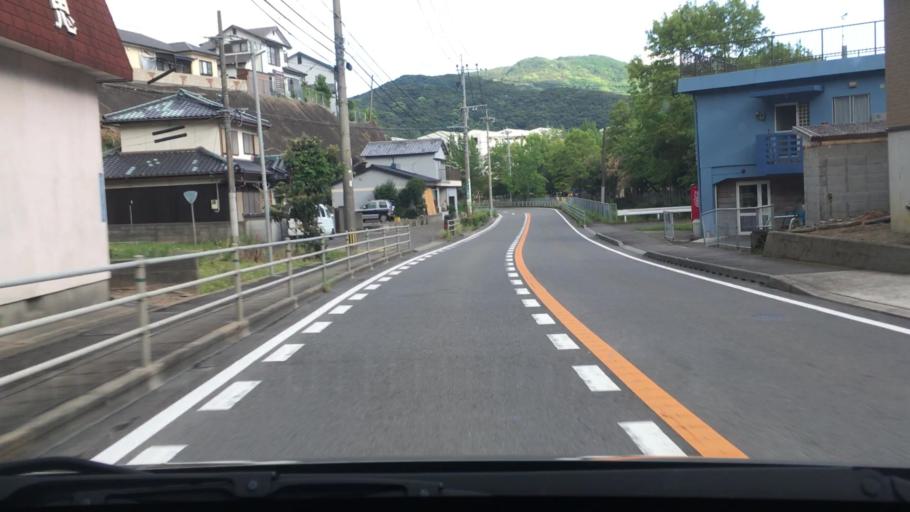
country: JP
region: Nagasaki
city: Togitsu
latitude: 32.8265
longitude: 129.7729
